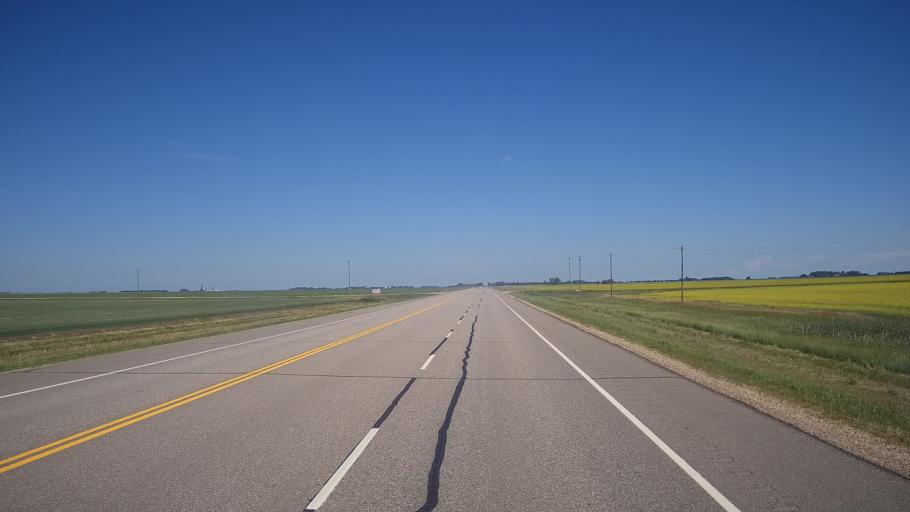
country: CA
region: Manitoba
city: Portage la Prairie
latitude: 50.0168
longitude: -98.4688
